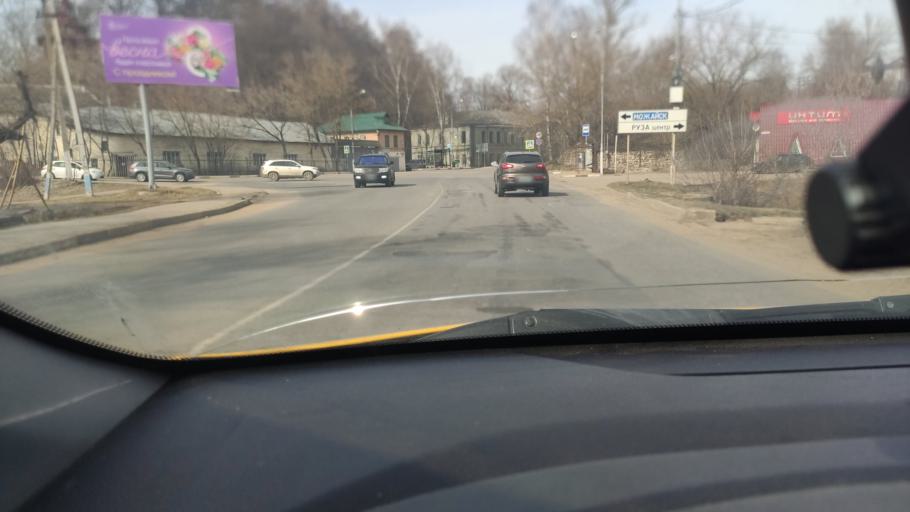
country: RU
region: Moskovskaya
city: Ruza
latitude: 55.6970
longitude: 36.1951
